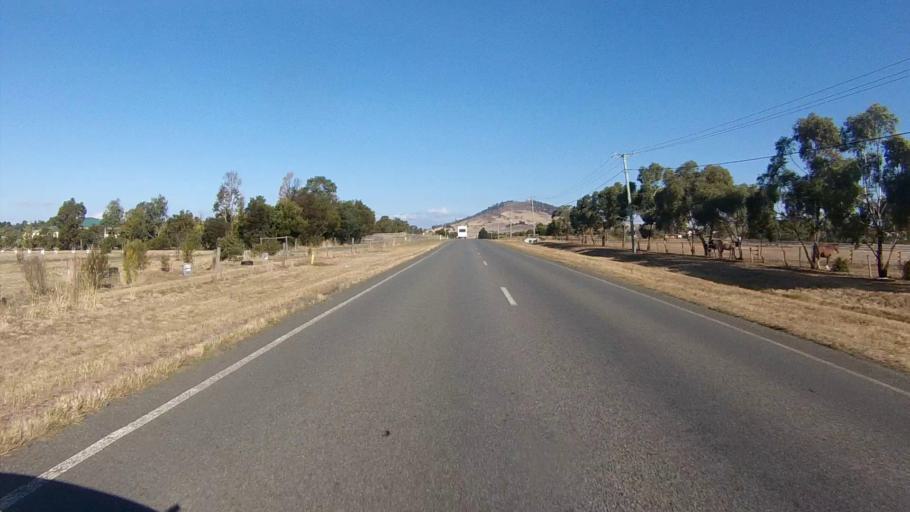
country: AU
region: Tasmania
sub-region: Clarence
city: Seven Mile Beach
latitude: -42.8504
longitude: 147.4843
